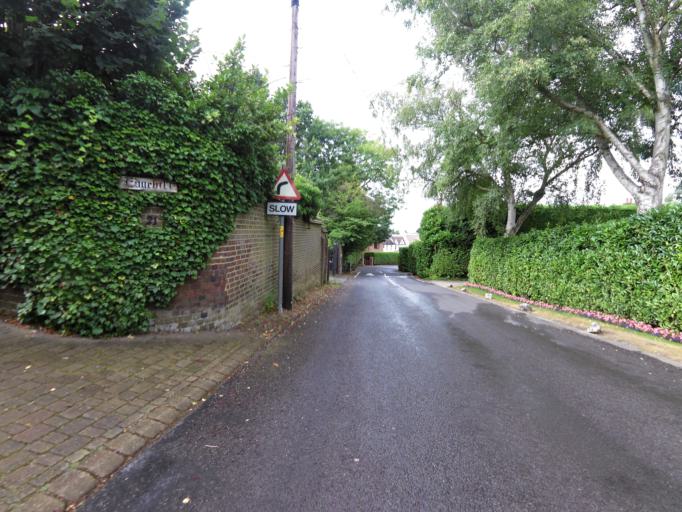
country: GB
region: England
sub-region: Hertfordshire
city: Radlett
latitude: 51.6909
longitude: -0.3159
